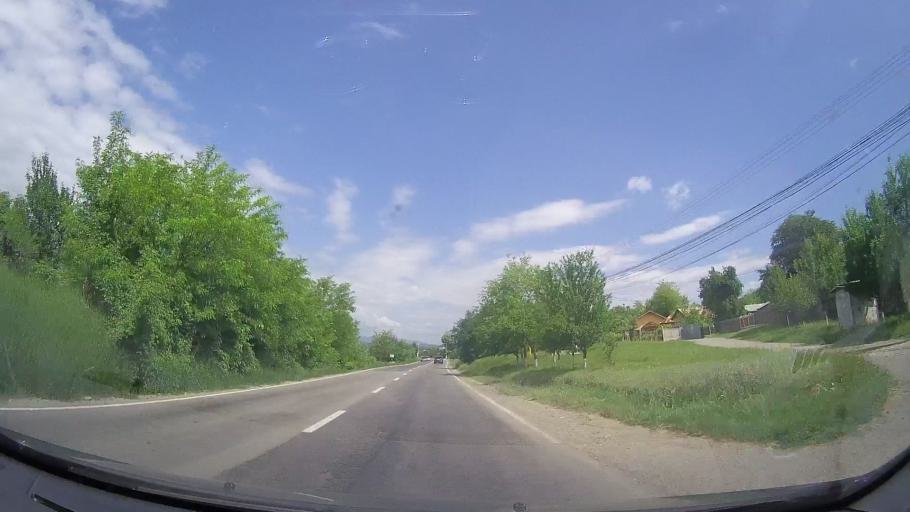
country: RO
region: Prahova
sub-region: Comuna Gura Vitioarei
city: Fagetu
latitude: 45.1269
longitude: 26.0354
